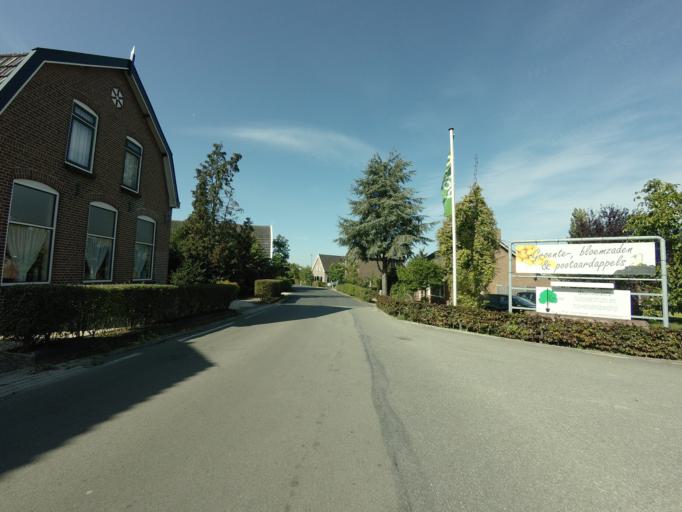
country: NL
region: South Holland
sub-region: Gemeente Gorinchem
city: Gorinchem
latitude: 51.8741
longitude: 4.9906
